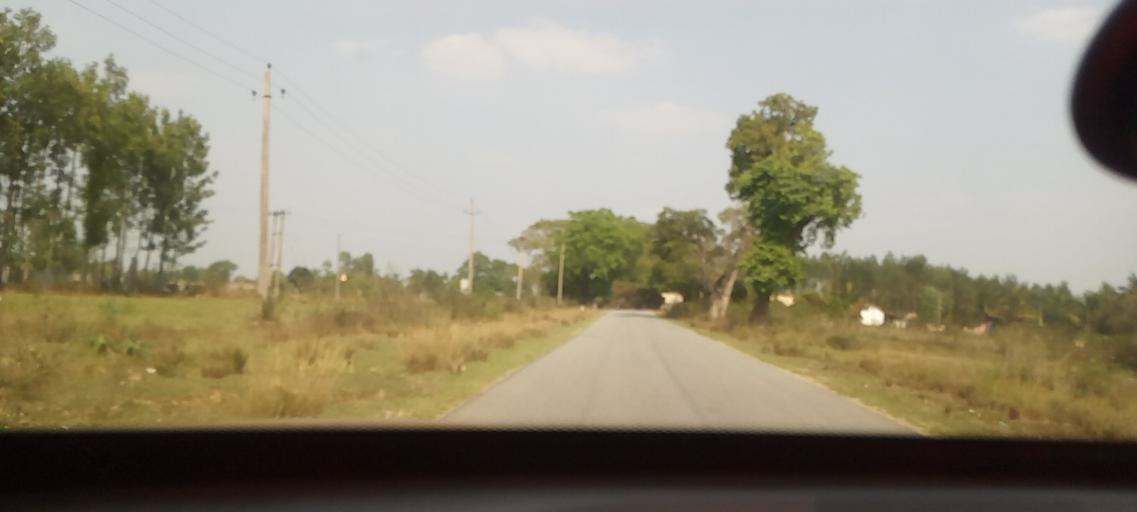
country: IN
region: Karnataka
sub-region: Hassan
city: Belur
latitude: 13.1777
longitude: 75.8223
